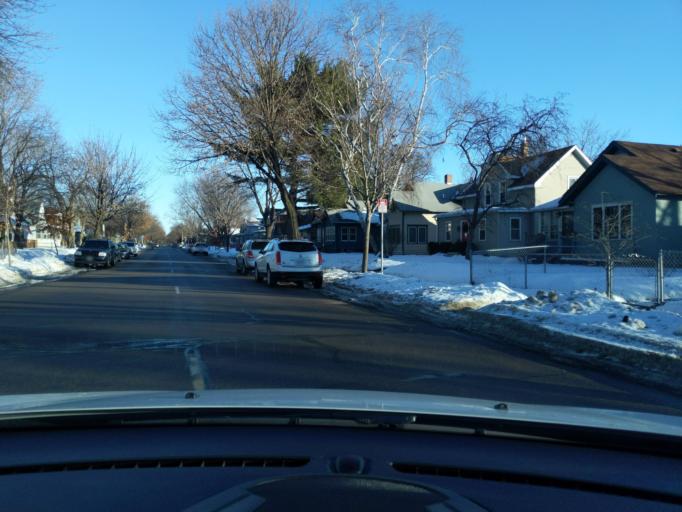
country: US
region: Minnesota
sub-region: Ramsey County
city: Lauderdale
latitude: 44.9271
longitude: -93.2128
